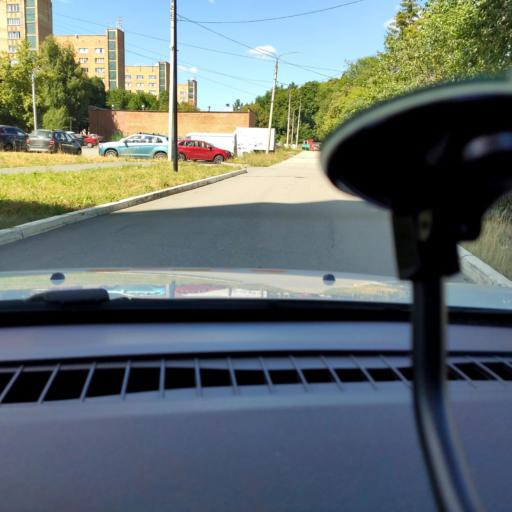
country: RU
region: Samara
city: Samara
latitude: 53.2587
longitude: 50.2481
